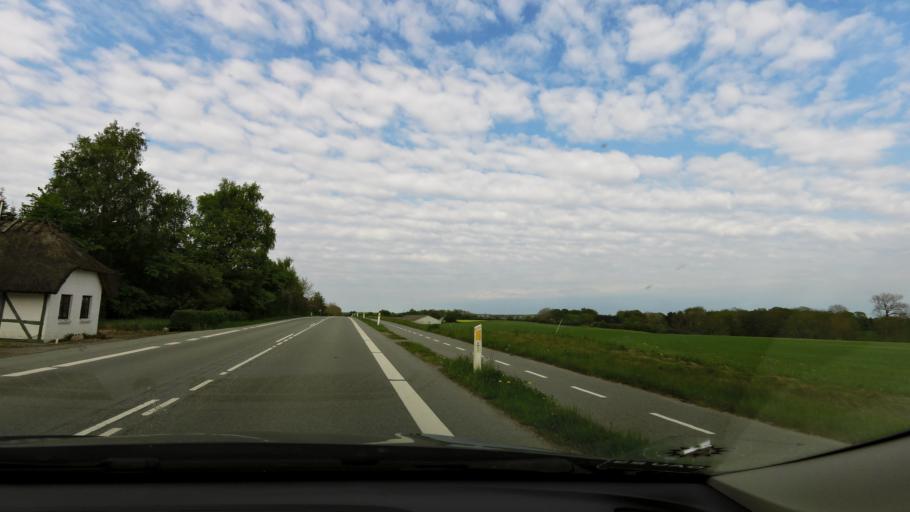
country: DK
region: South Denmark
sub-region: Nyborg Kommune
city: Nyborg
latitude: 55.2958
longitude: 10.7119
